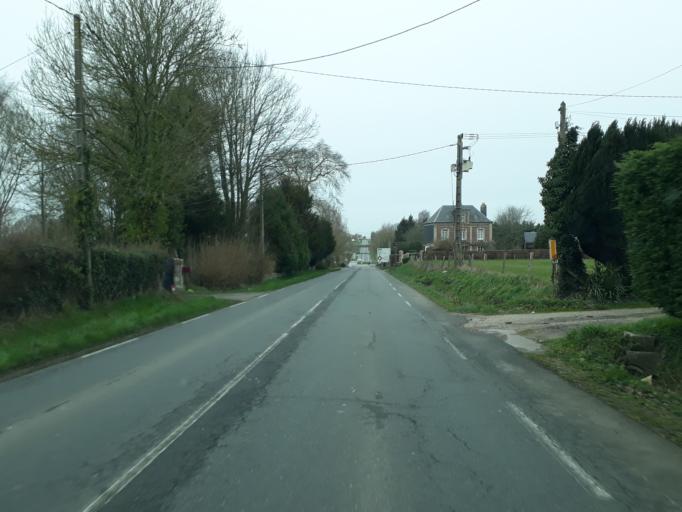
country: FR
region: Haute-Normandie
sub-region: Departement de la Seine-Maritime
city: Beuzeville-la-Grenier
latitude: 49.5988
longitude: 0.4186
